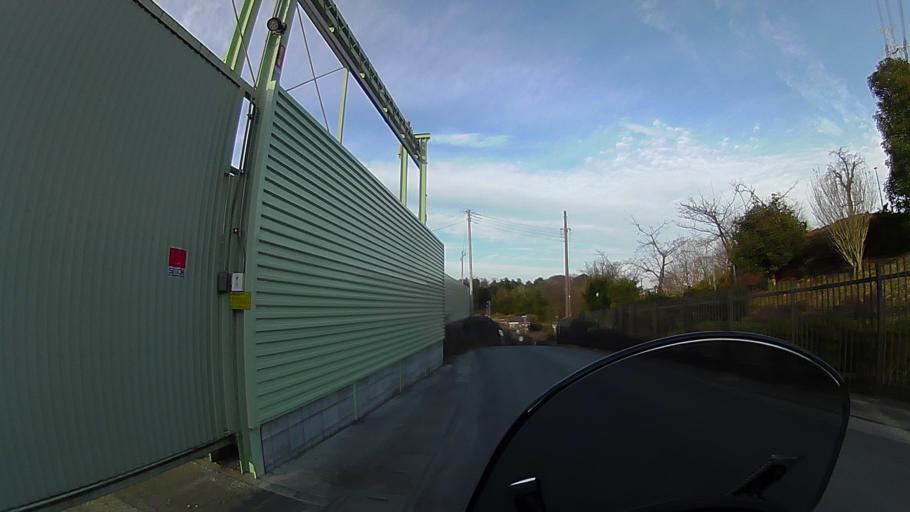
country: JP
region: Kanagawa
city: Atsugi
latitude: 35.4187
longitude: 139.4158
